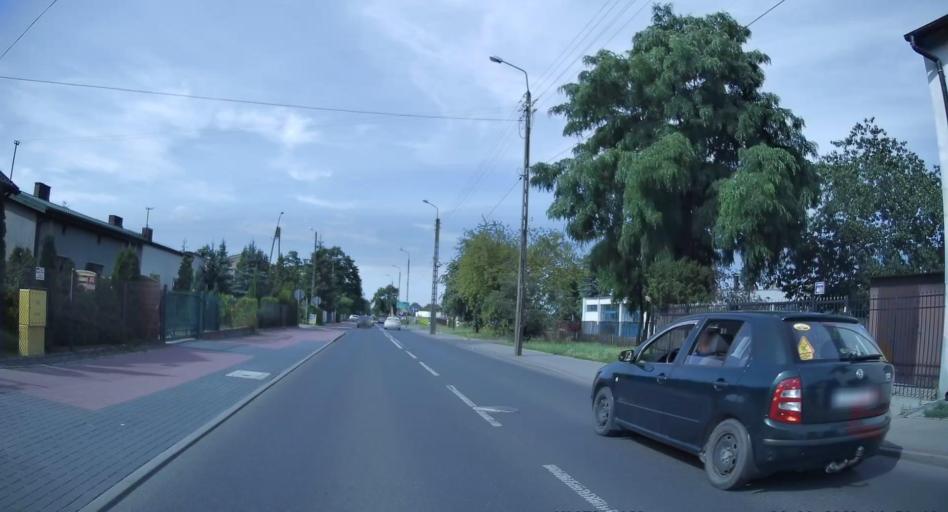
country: PL
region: Lodz Voivodeship
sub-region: Powiat tomaszowski
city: Tomaszow Mazowiecki
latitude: 51.5291
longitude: 19.9970
